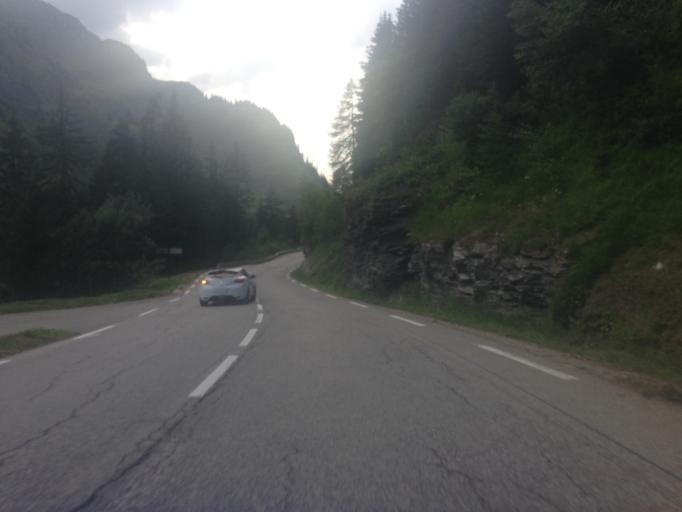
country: FR
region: Rhone-Alpes
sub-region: Departement de la Savoie
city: Tignes
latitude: 45.5230
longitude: 6.9136
